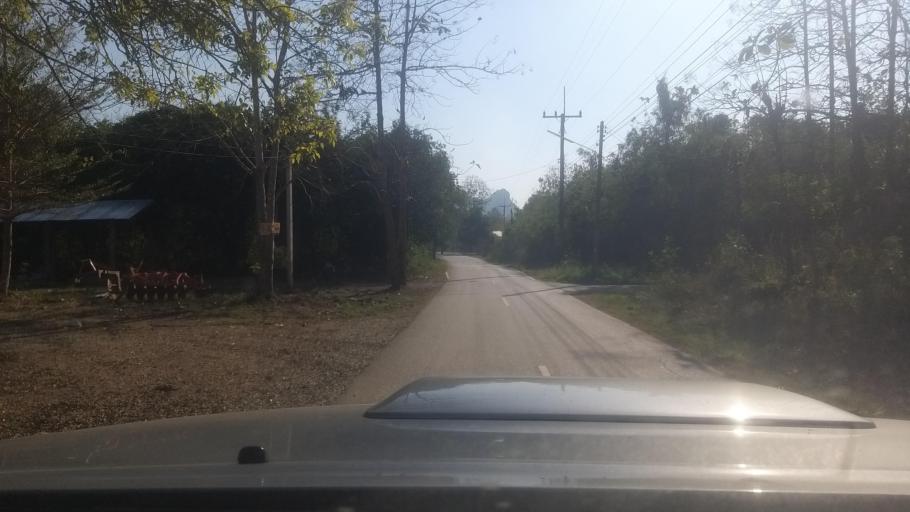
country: TH
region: Phrae
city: Phrae
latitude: 18.2551
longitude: 99.9951
